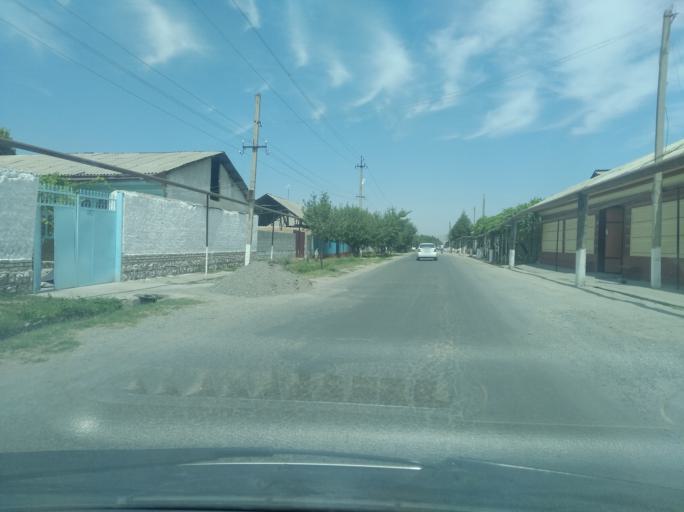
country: KG
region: Osh
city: Aravan
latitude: 40.6072
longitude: 72.4587
